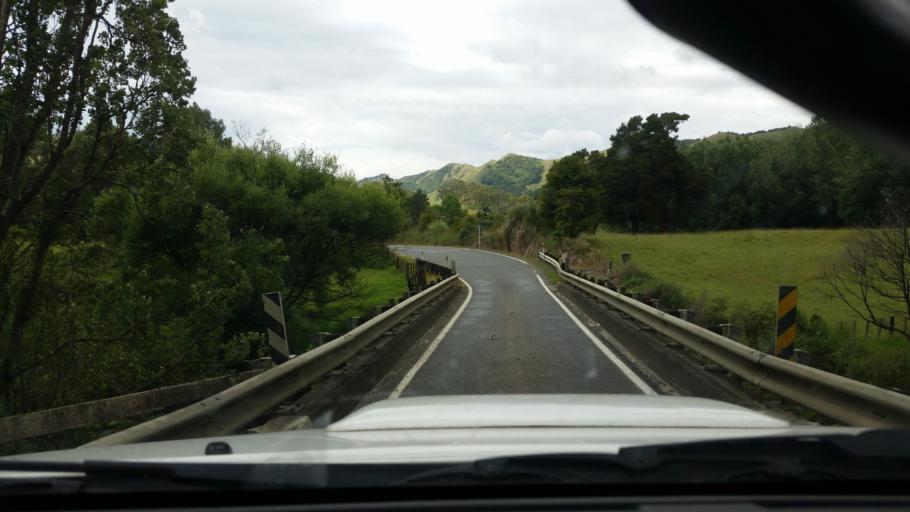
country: NZ
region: Northland
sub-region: Kaipara District
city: Dargaville
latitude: -35.7468
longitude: 173.8773
